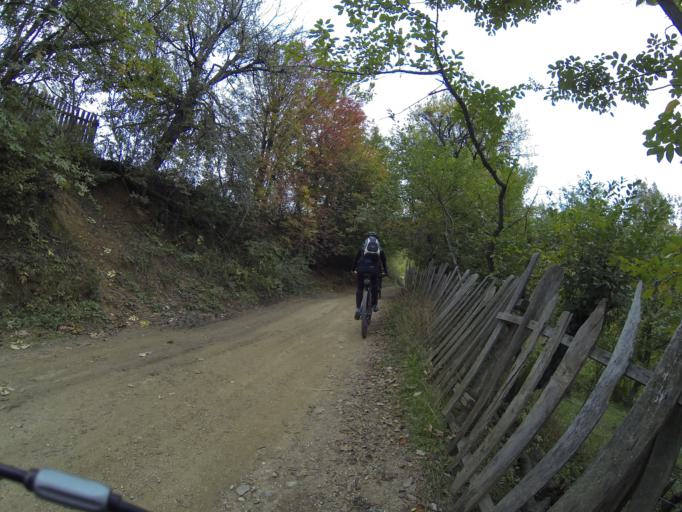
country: RO
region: Gorj
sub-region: Comuna Tismana
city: Sohodol
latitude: 45.0635
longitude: 22.8718
